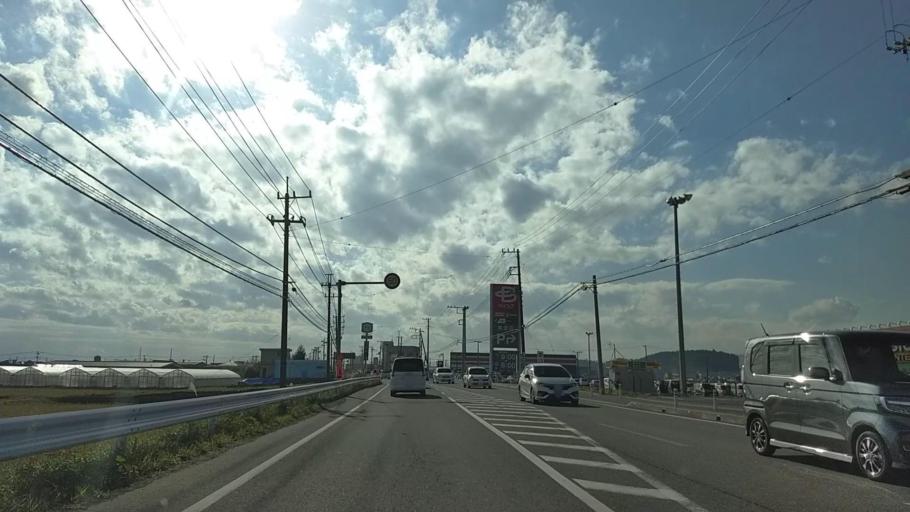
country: JP
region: Chiba
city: Togane
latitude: 35.5801
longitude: 140.3840
